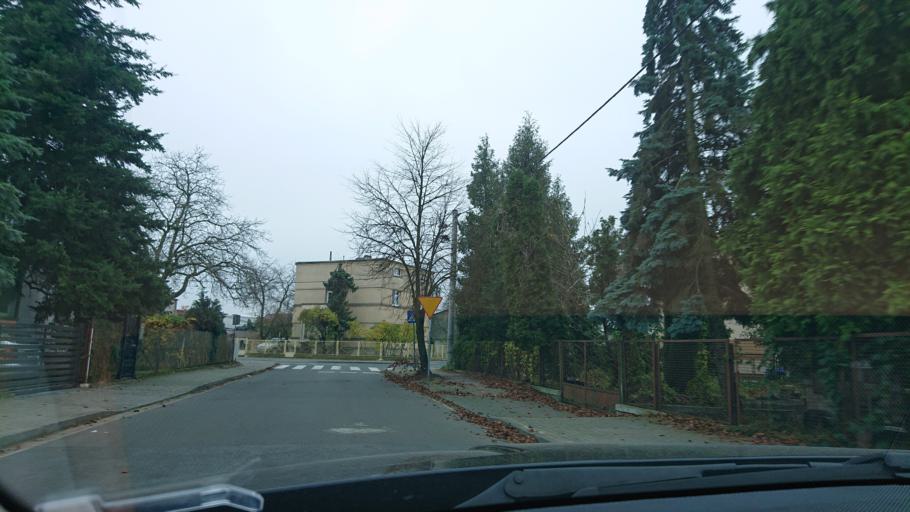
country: PL
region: Greater Poland Voivodeship
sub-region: Powiat gnieznienski
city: Gniezno
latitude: 52.5360
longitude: 17.6245
